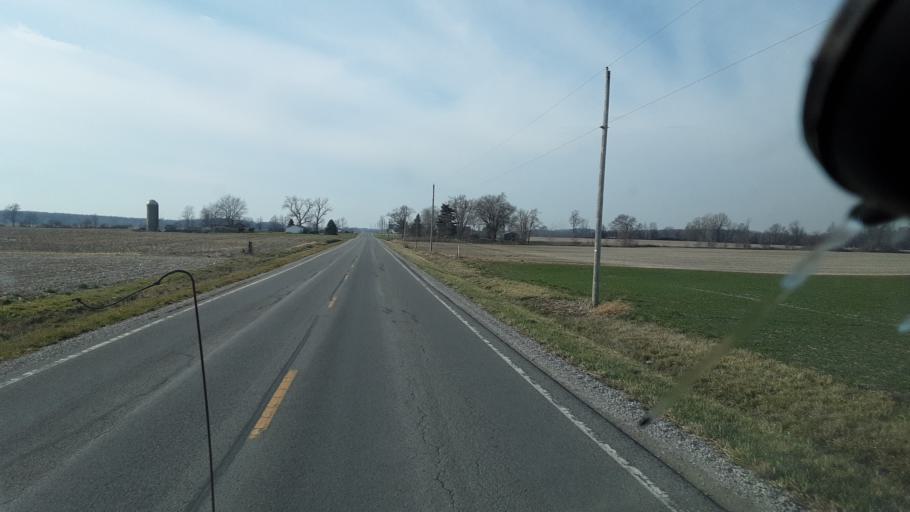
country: US
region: Ohio
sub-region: Williams County
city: Edgerton
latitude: 41.3827
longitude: -84.7521
